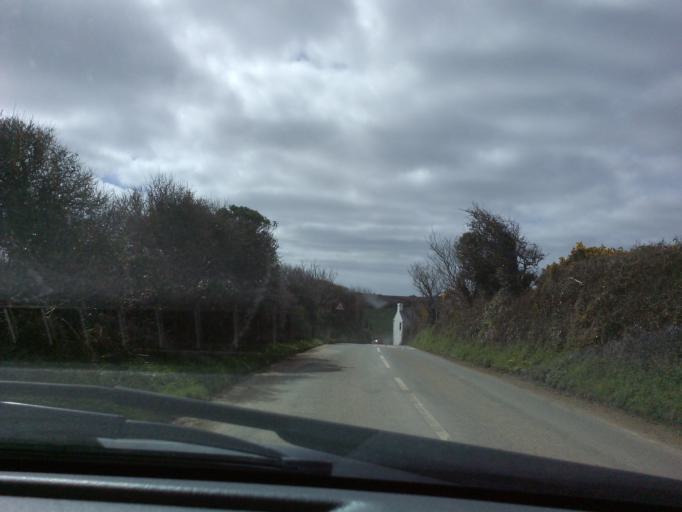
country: GB
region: England
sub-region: Cornwall
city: St. Buryan
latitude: 50.0600
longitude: -5.6066
